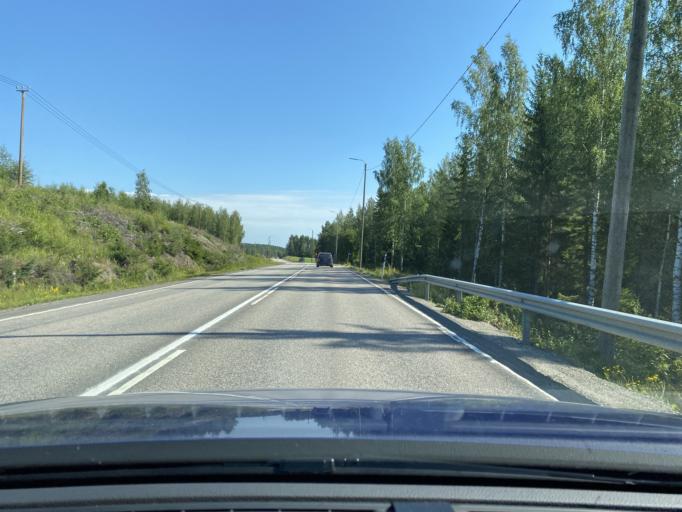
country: FI
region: Central Finland
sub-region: Jaemsae
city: Jaemsae
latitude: 61.8742
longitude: 25.2472
